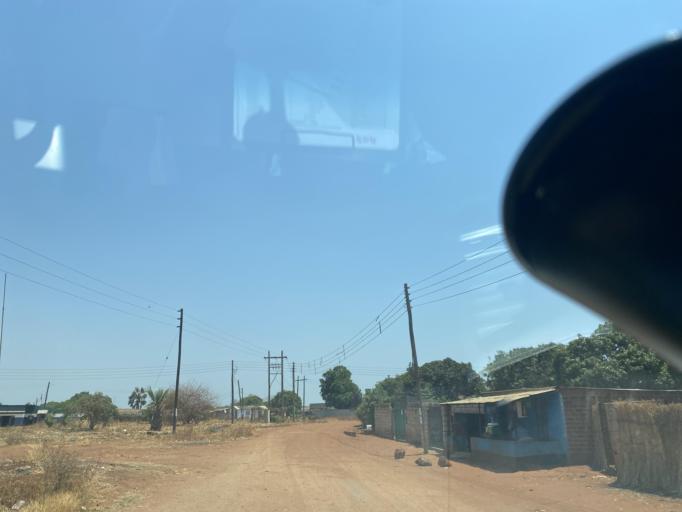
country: ZM
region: Southern
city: Nakambala
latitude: -15.5067
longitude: 27.9283
